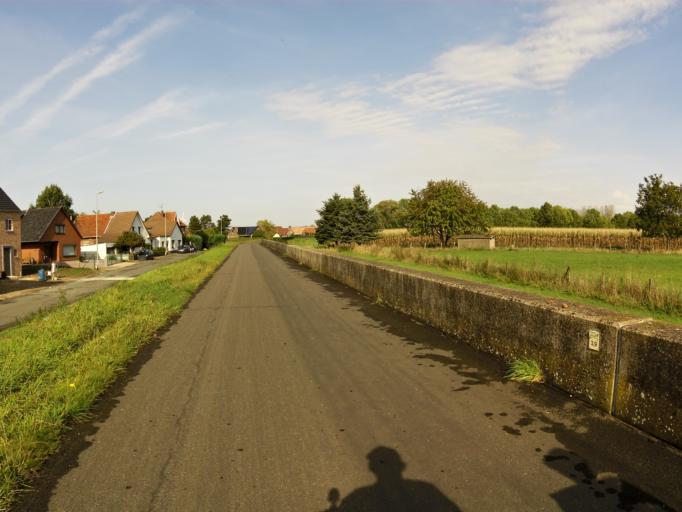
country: NL
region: Limburg
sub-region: Gemeente Stein
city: Elsloo
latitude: 50.9334
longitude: 5.7323
